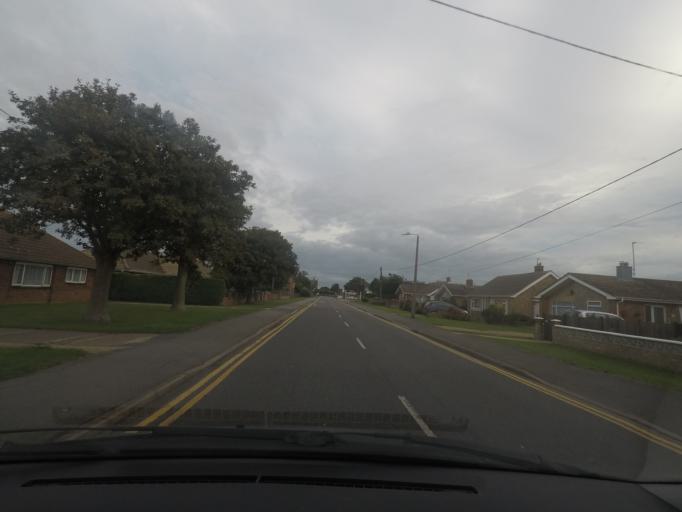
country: GB
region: England
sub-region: Lincolnshire
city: Chapel Saint Leonards
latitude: 53.2252
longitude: 0.3365
